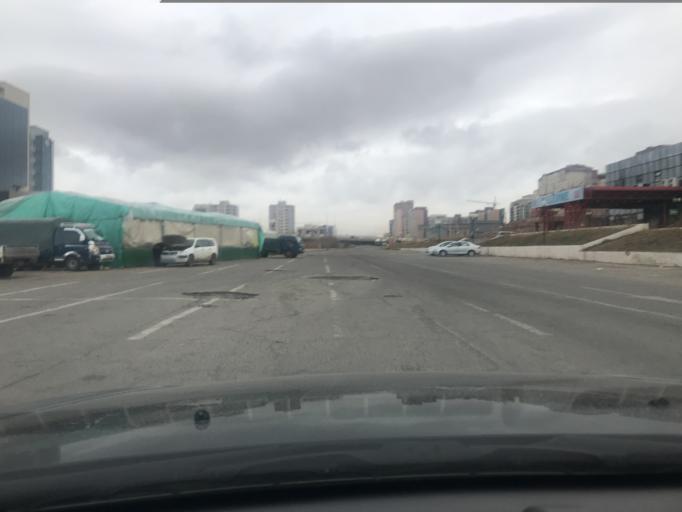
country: MN
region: Ulaanbaatar
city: Ulaanbaatar
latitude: 47.9213
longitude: 106.9322
